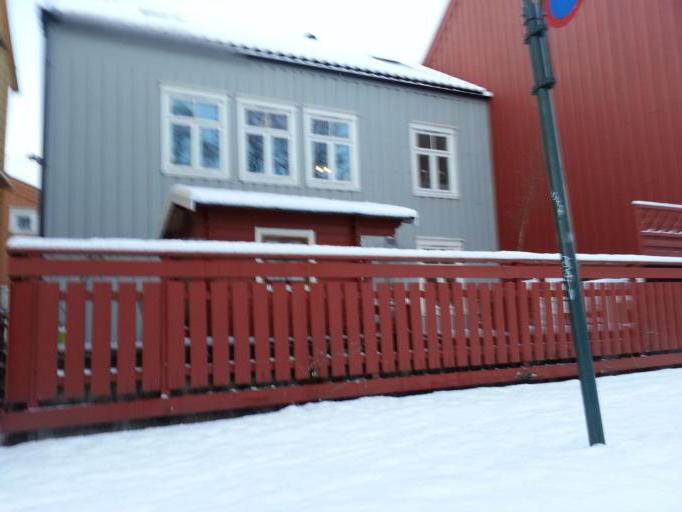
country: NO
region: Sor-Trondelag
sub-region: Trondheim
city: Trondheim
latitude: 63.4300
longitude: 10.4053
